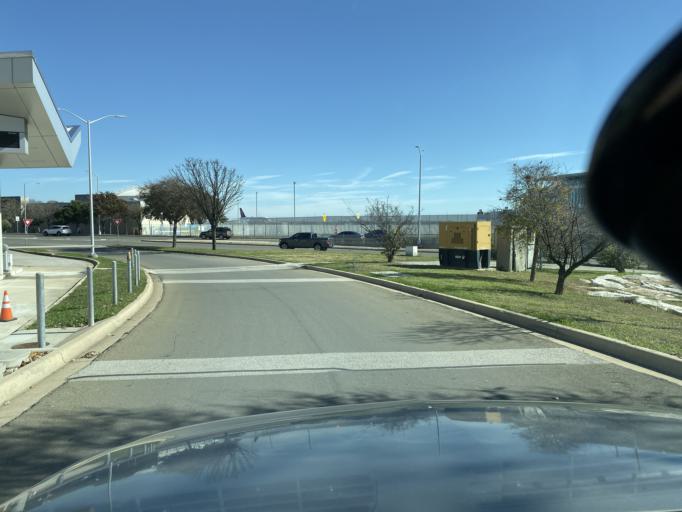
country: US
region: Texas
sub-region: Travis County
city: Hornsby Bend
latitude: 30.2040
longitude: -97.6648
